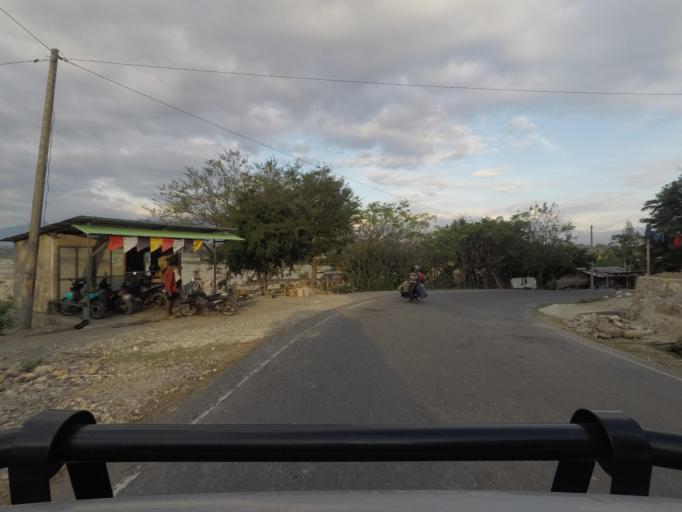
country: TL
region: Bobonaro
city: Maliana
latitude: -8.9523
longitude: 125.1100
